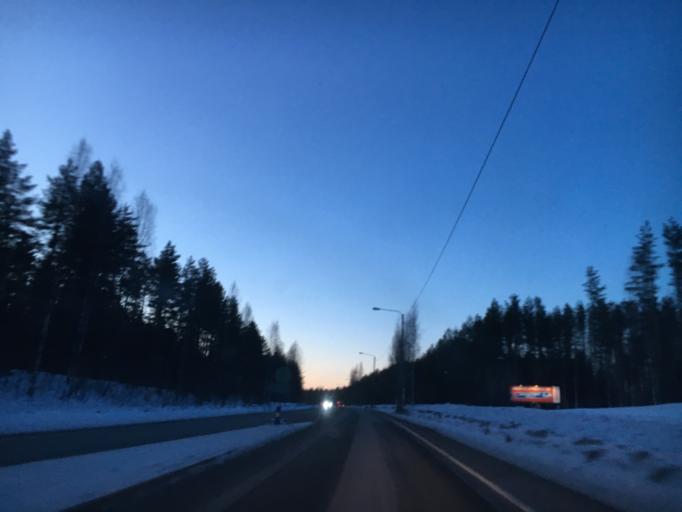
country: FI
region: Kainuu
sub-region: Kajaani
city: Kajaani
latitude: 64.1973
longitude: 27.7501
